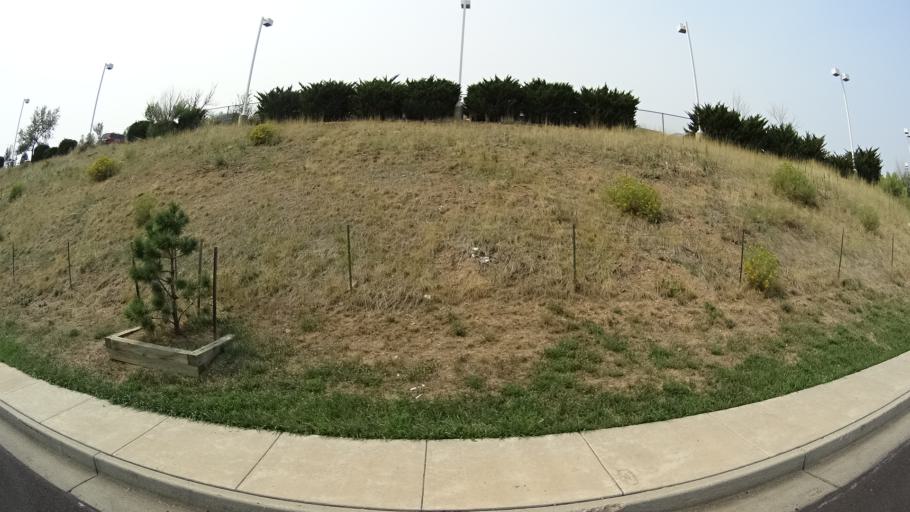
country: US
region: Colorado
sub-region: El Paso County
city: Colorado Springs
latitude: 38.8169
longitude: -104.8387
